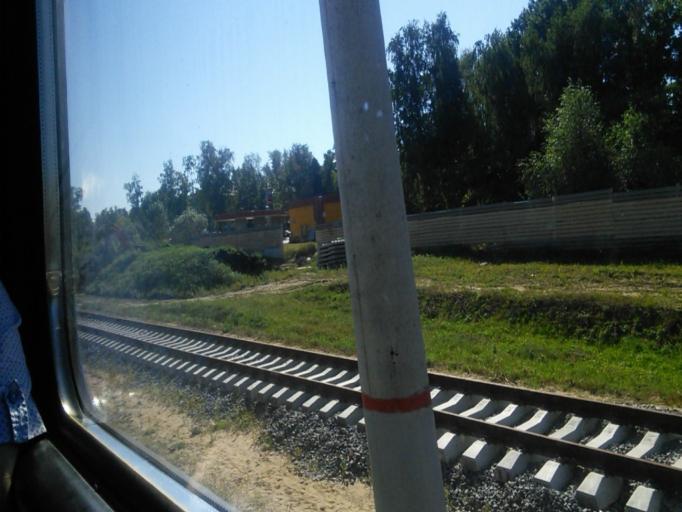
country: RU
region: Moskovskaya
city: Saltykovka
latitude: 55.7516
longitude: 37.9683
